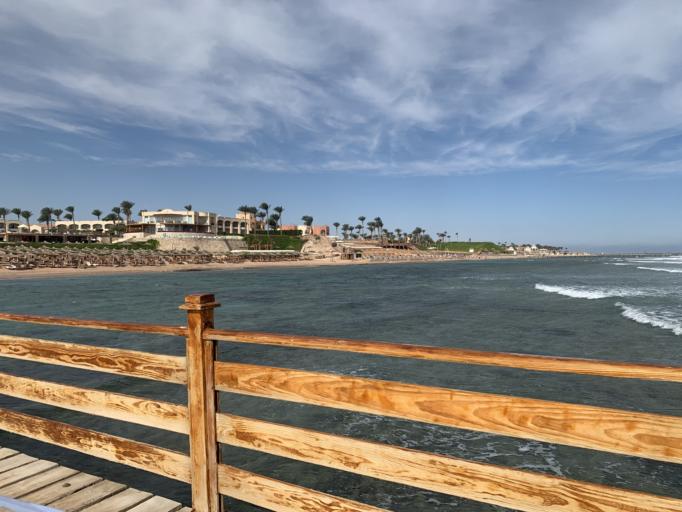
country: EG
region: South Sinai
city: Sharm el-Sheikh
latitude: 28.0207
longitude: 34.4413
